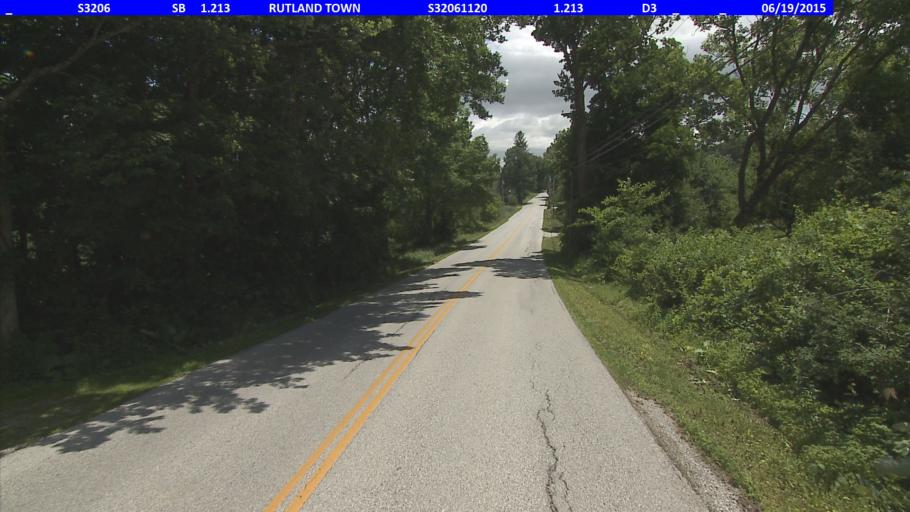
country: US
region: Vermont
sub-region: Rutland County
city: Rutland
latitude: 43.6463
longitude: -72.9953
